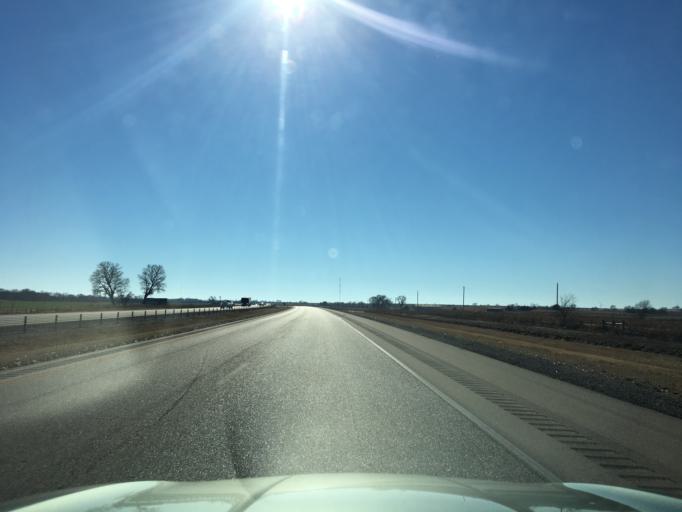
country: US
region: Oklahoma
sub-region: Kay County
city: Blackwell
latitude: 36.9010
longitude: -97.3542
